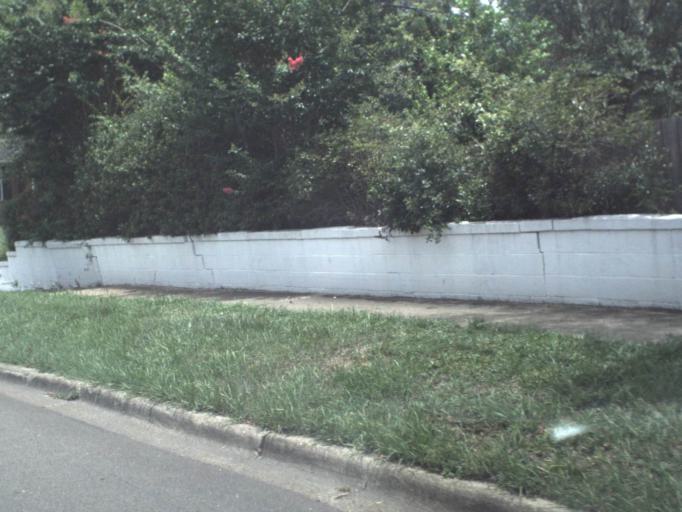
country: US
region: Florida
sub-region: Duval County
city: Jacksonville
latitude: 30.2949
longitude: -81.6477
